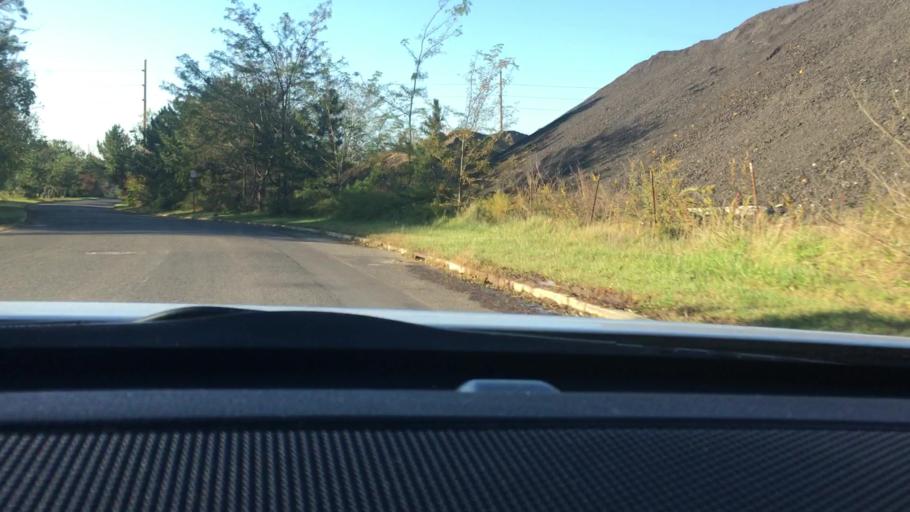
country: US
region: New Jersey
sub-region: Atlantic County
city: Pleasantville
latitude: 39.4010
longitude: -74.5352
